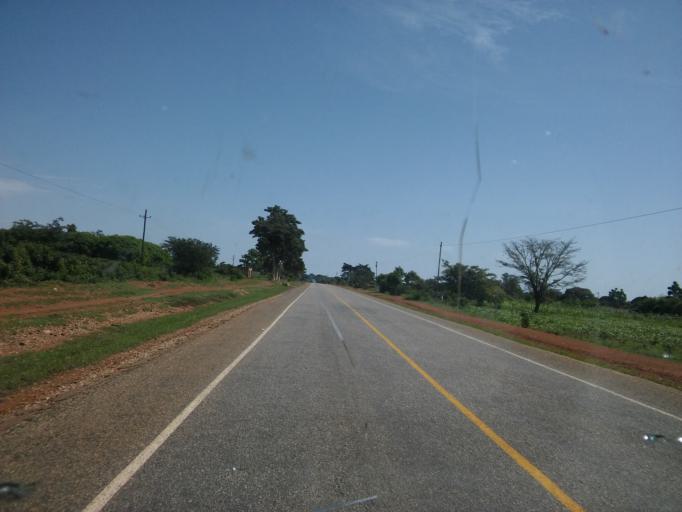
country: UG
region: Eastern Region
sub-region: Bukedea District
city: Bukedea
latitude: 1.3822
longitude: 34.0122
